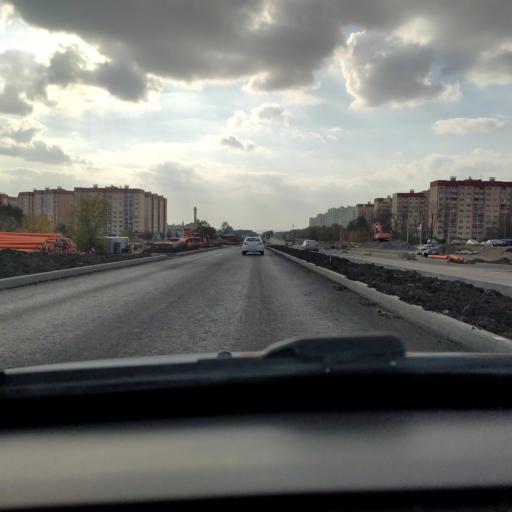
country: RU
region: Voronezj
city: Shilovo
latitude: 51.5647
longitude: 39.1215
